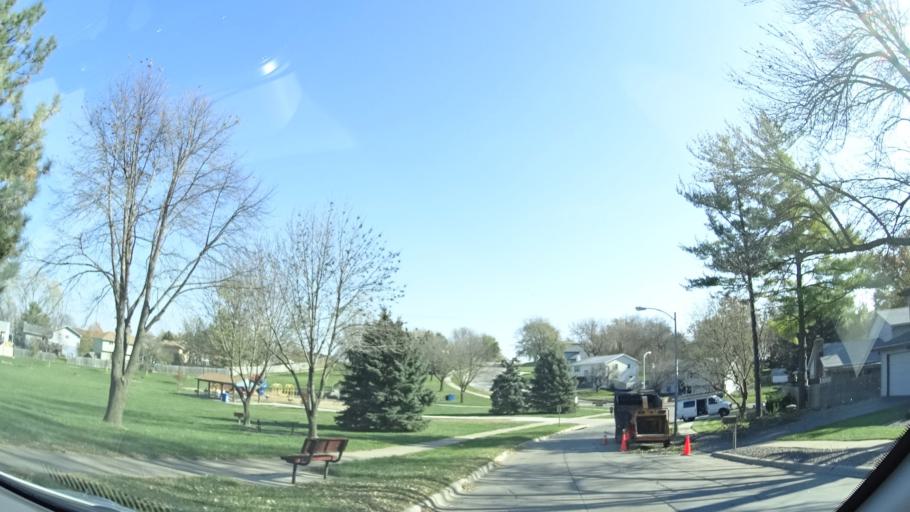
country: US
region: Nebraska
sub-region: Sarpy County
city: Offutt Air Force Base
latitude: 41.1355
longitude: -95.9640
